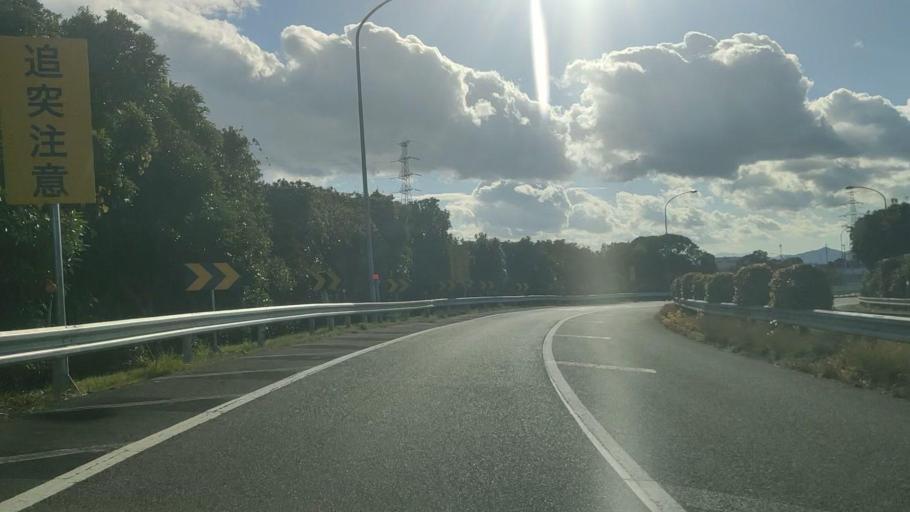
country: JP
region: Fukuoka
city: Nogata
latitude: 33.7834
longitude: 130.7462
